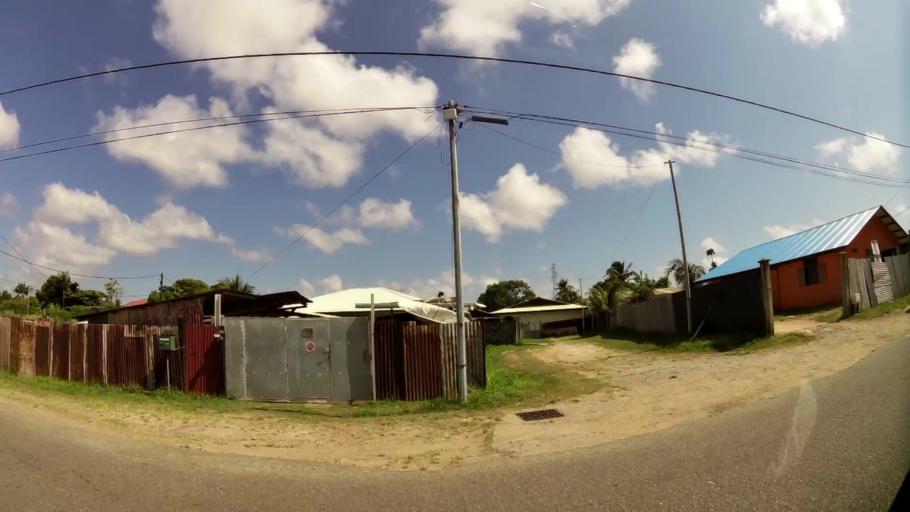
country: GF
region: Guyane
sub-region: Guyane
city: Cayenne
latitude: 4.9251
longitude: -52.3169
